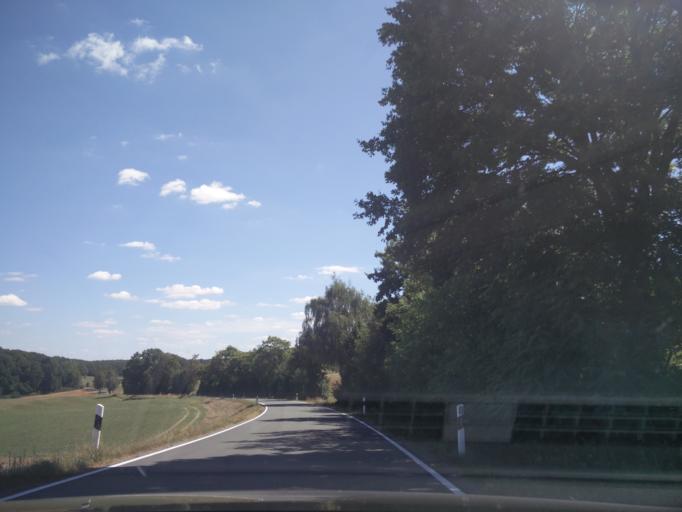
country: DE
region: North Rhine-Westphalia
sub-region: Regierungsbezirk Detmold
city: Willebadessen
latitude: 51.6619
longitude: 9.0233
